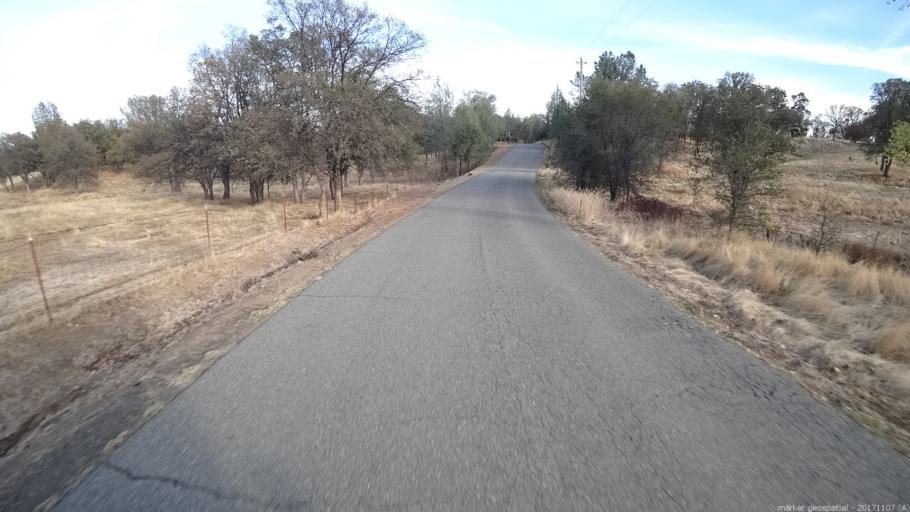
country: US
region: California
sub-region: Shasta County
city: Shasta
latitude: 40.5268
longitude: -122.4777
